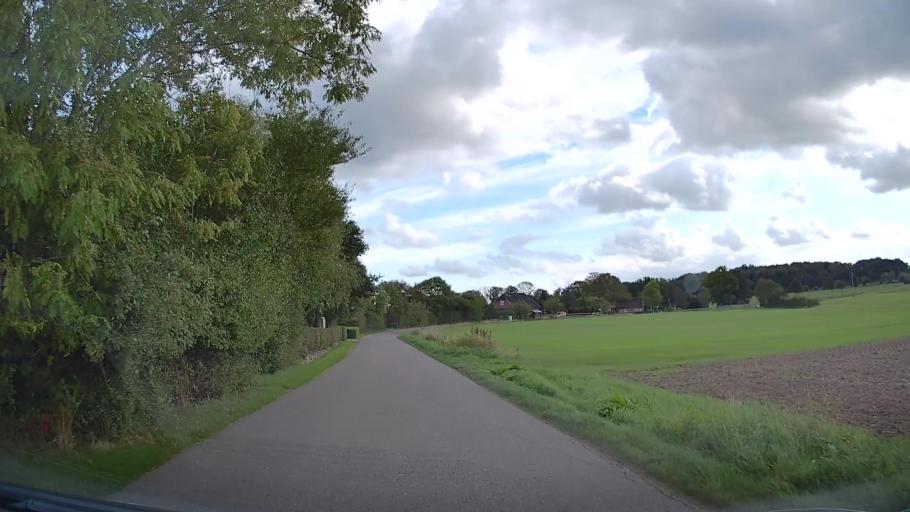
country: DE
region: Schleswig-Holstein
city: Steinberg
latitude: 54.7801
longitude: 9.7819
